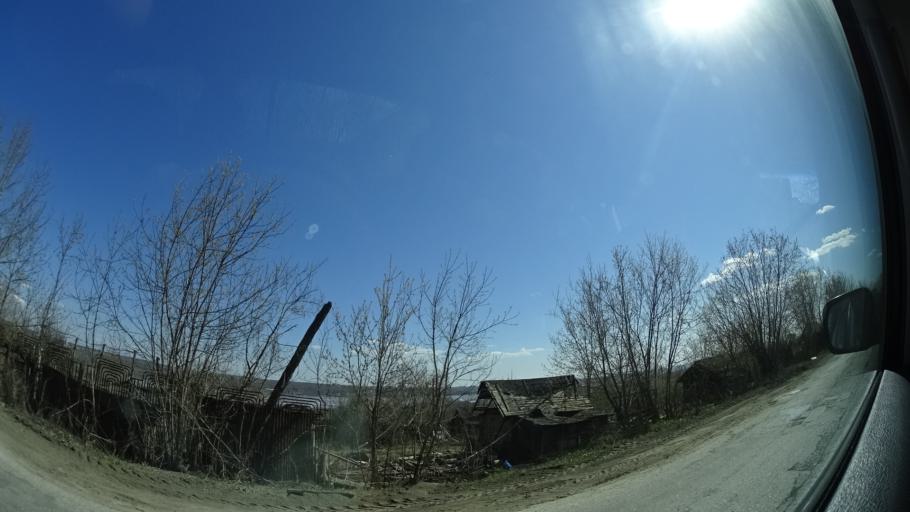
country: RU
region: Perm
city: Perm
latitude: 58.1107
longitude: 56.3165
